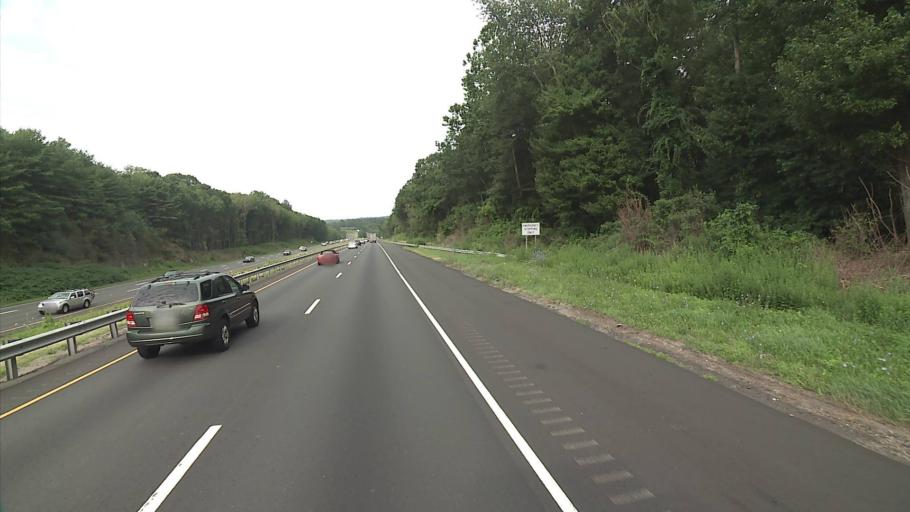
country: US
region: Connecticut
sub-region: New Haven County
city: Middlebury
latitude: 41.5119
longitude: -73.1289
